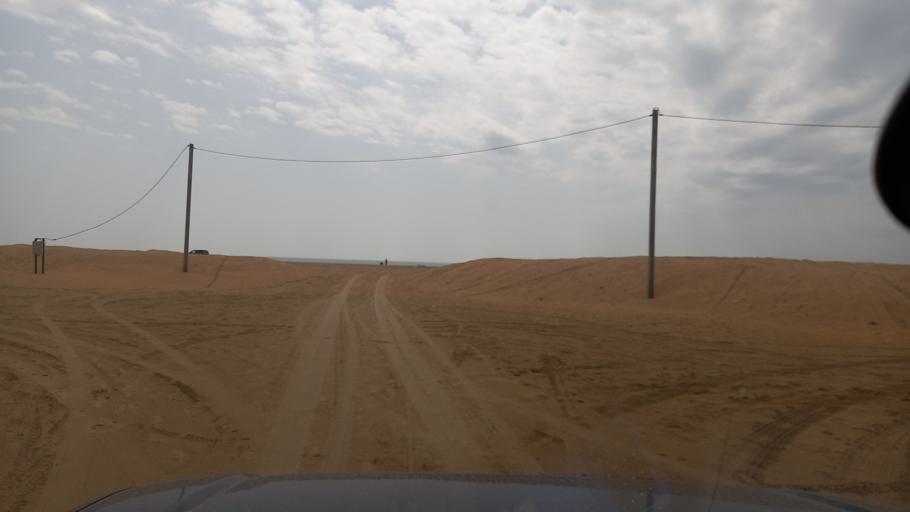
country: RU
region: Krasnodarskiy
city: Vityazevo
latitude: 44.9915
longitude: 37.2342
